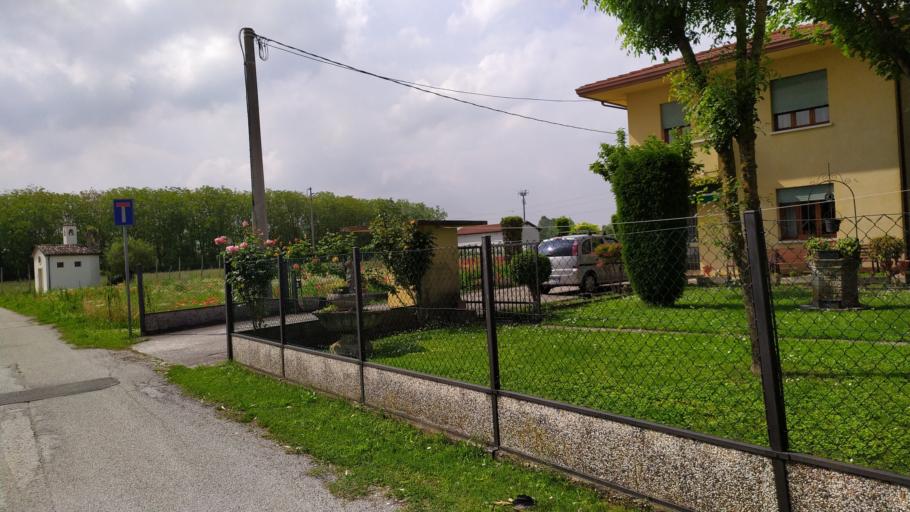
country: IT
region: Veneto
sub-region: Provincia di Padova
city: Vigodarzere
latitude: 45.4578
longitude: 11.8940
